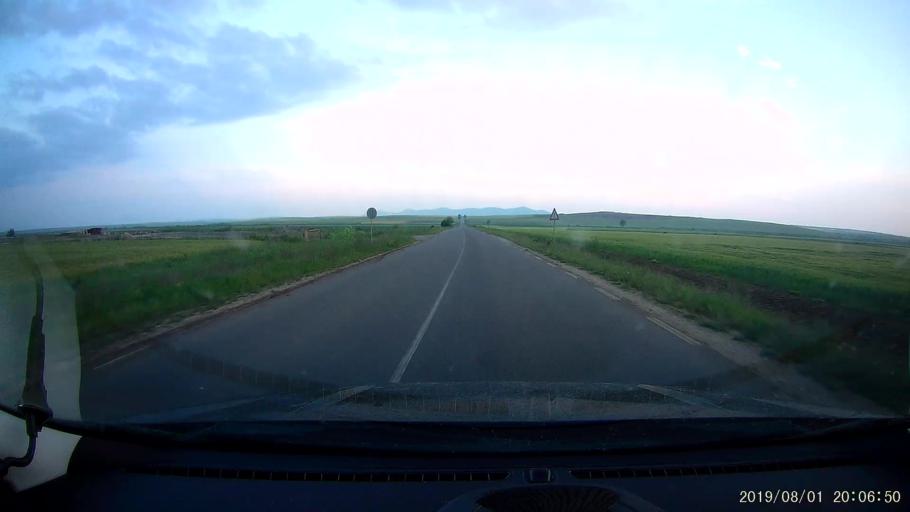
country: BG
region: Yambol
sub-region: Obshtina Yambol
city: Yambol
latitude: 42.5303
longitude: 26.5585
